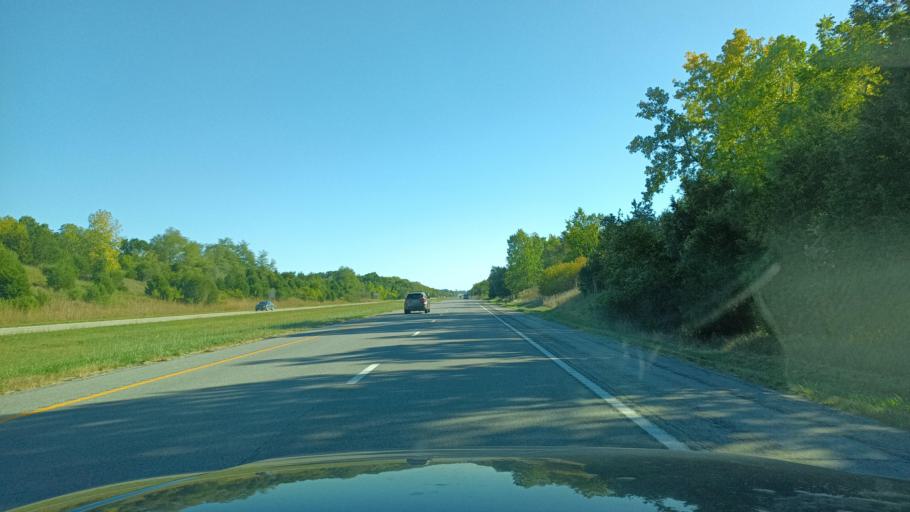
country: US
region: Missouri
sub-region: Boone County
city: Hallsville
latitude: 39.0806
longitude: -92.3301
